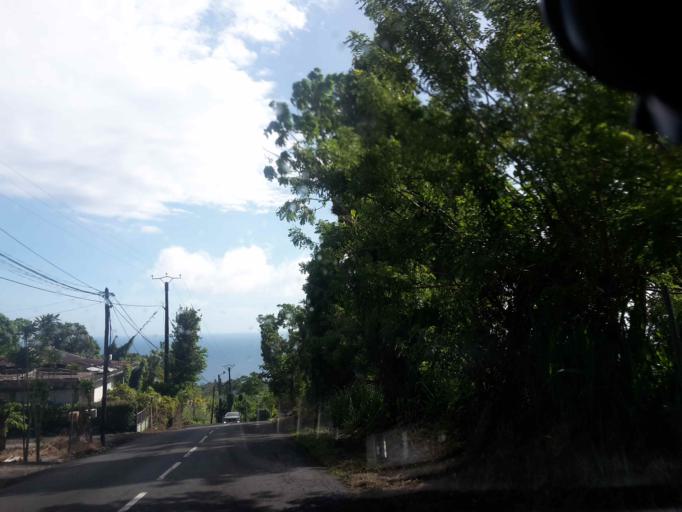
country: GP
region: Guadeloupe
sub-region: Guadeloupe
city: Gourbeyre
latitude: 16.0093
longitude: -61.6947
